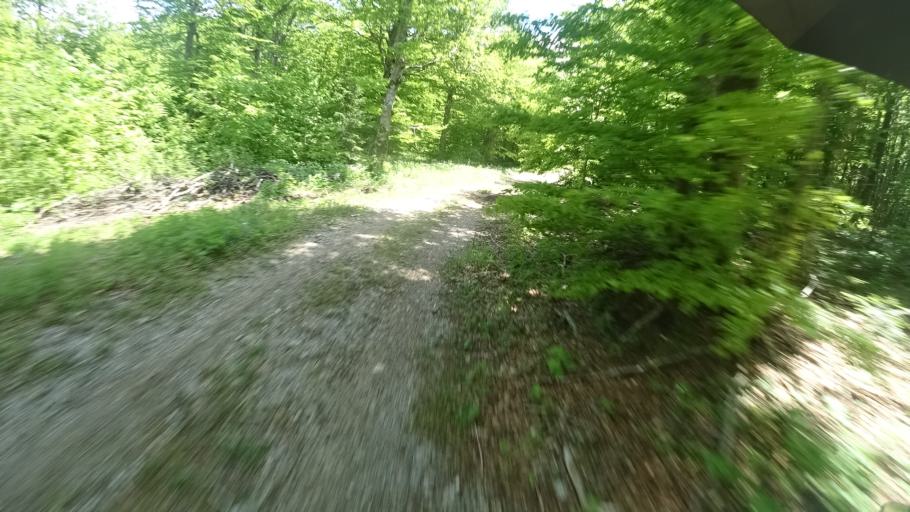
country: HR
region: Zadarska
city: Gracac
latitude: 44.4664
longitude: 15.9012
